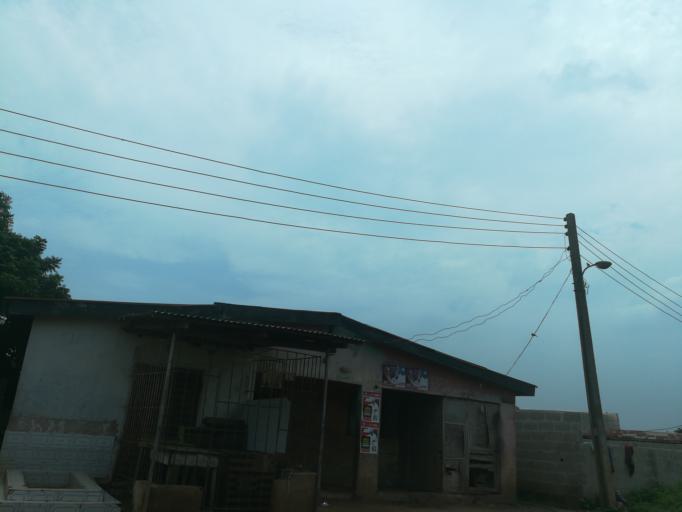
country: NG
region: Lagos
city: Ikorodu
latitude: 6.5832
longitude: 3.5946
